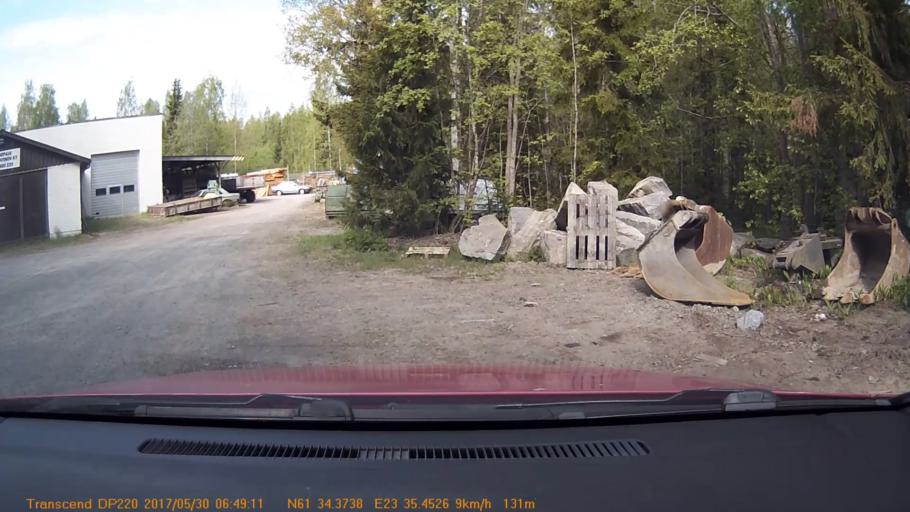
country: FI
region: Pirkanmaa
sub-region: Tampere
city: Yloejaervi
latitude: 61.5730
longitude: 23.5910
